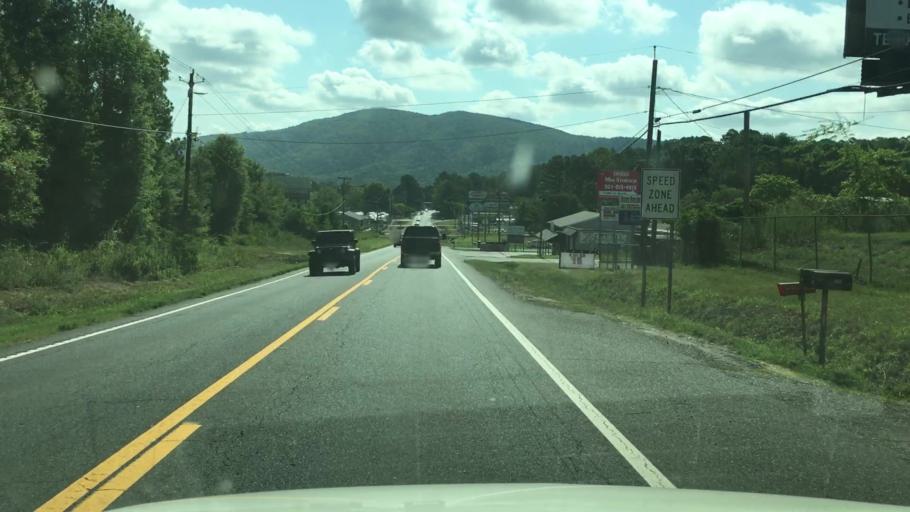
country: US
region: Arkansas
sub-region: Garland County
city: Piney
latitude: 34.5079
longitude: -93.1379
